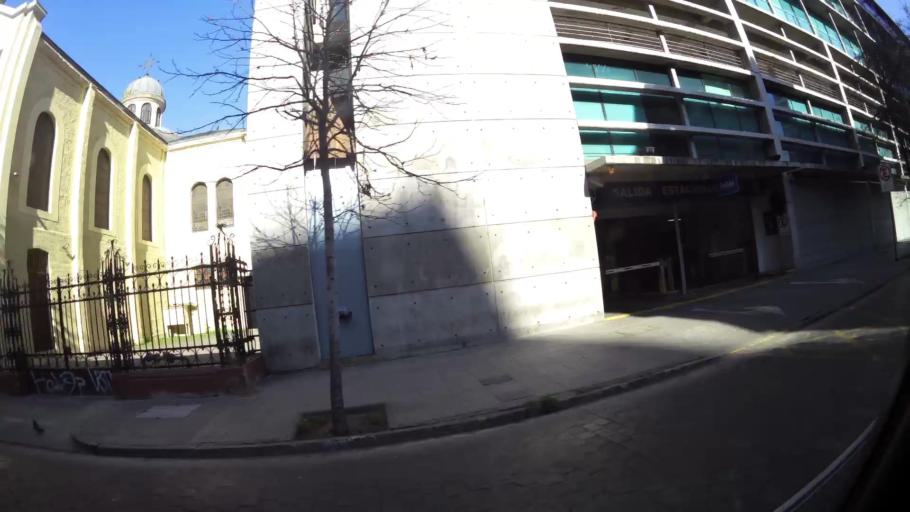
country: CL
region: Santiago Metropolitan
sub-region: Provincia de Santiago
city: Santiago
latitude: -33.4440
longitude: -70.6408
